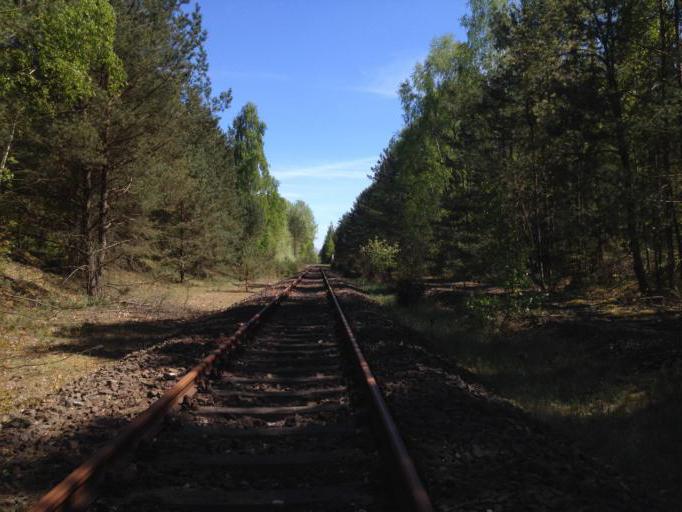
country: DE
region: Brandenburg
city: Templin
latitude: 53.1436
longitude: 13.4161
